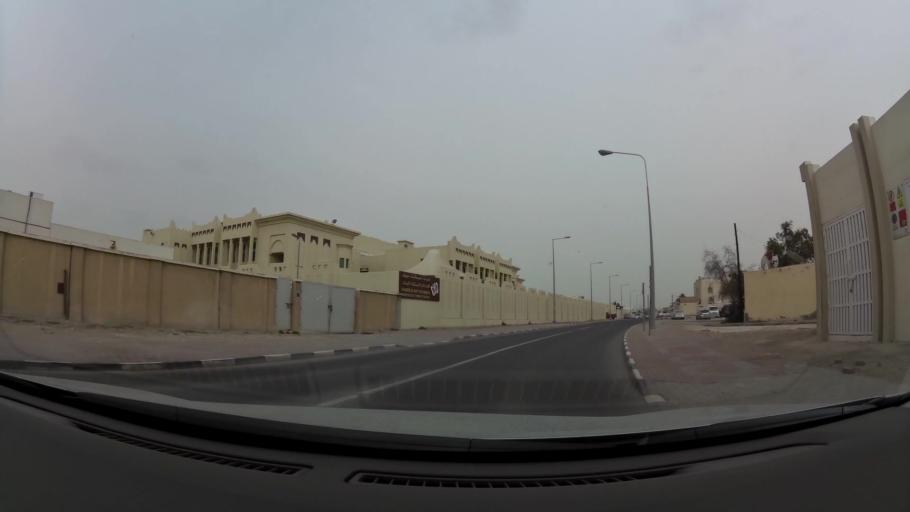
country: QA
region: Baladiyat ad Dawhah
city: Doha
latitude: 25.2524
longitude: 51.5009
